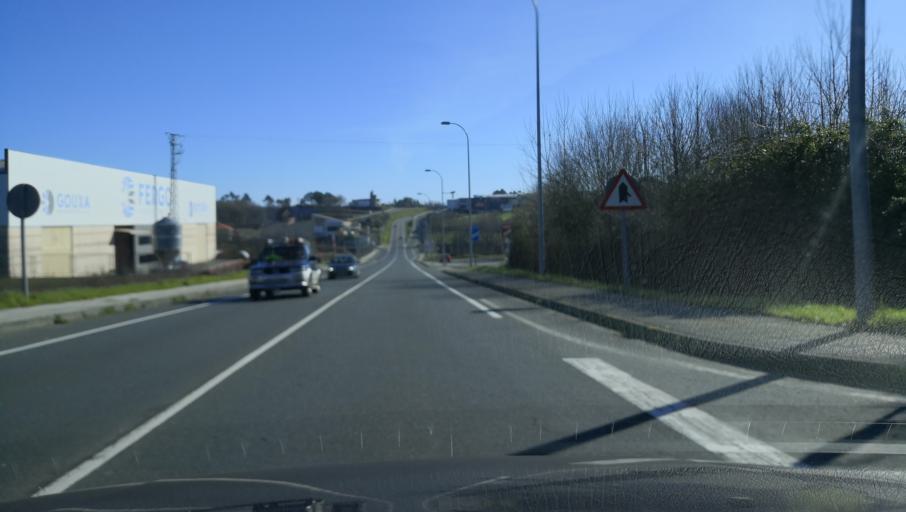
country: ES
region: Galicia
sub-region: Provincia de Pontevedra
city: Silleda
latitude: 42.6949
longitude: -8.2345
